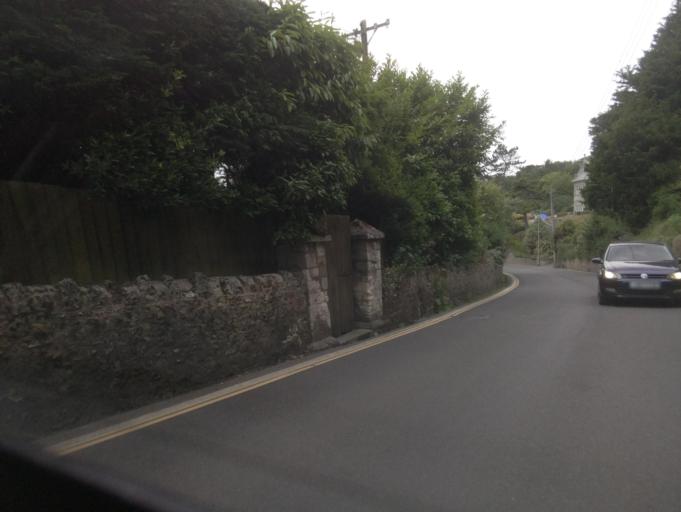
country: GB
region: England
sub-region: Devon
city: Colyton
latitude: 50.7001
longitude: -3.0922
